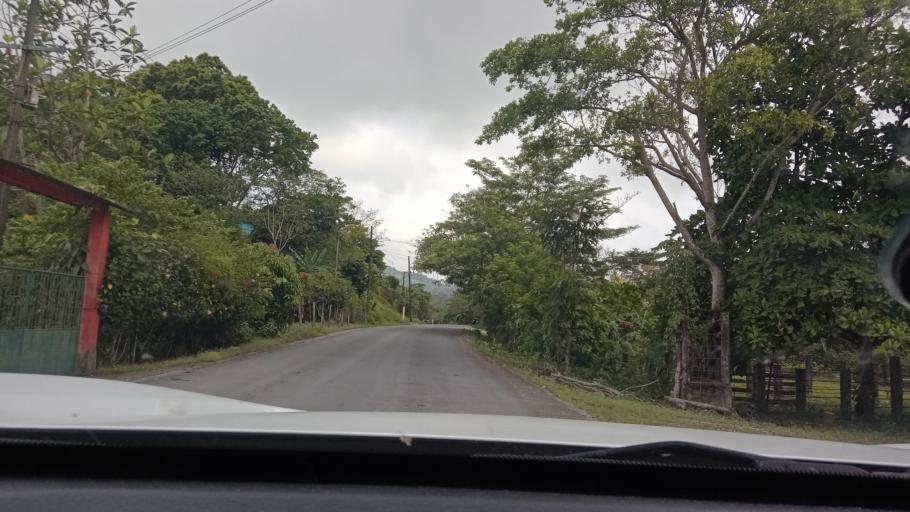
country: MX
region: Tabasco
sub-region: Huimanguillo
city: Francisco Rueda
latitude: 17.5292
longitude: -94.1264
